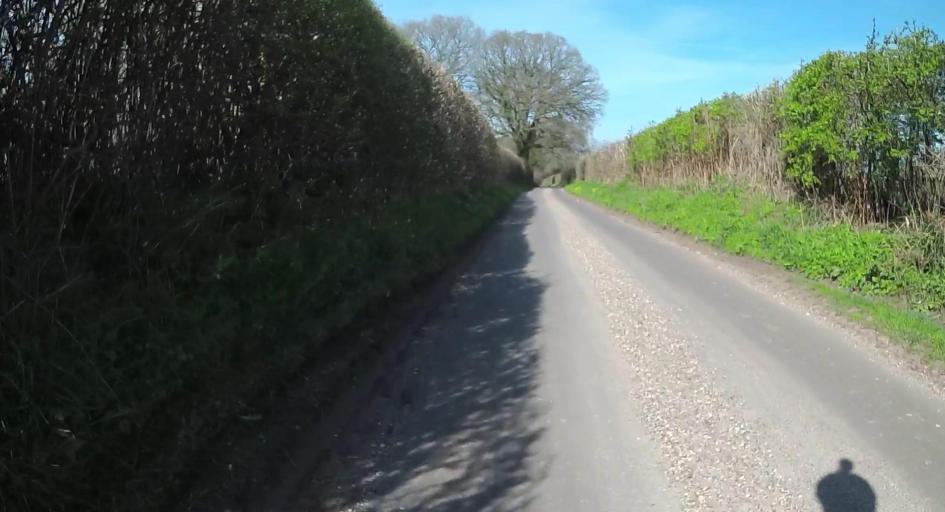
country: GB
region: England
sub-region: Hampshire
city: Highclere
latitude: 51.2790
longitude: -1.4087
